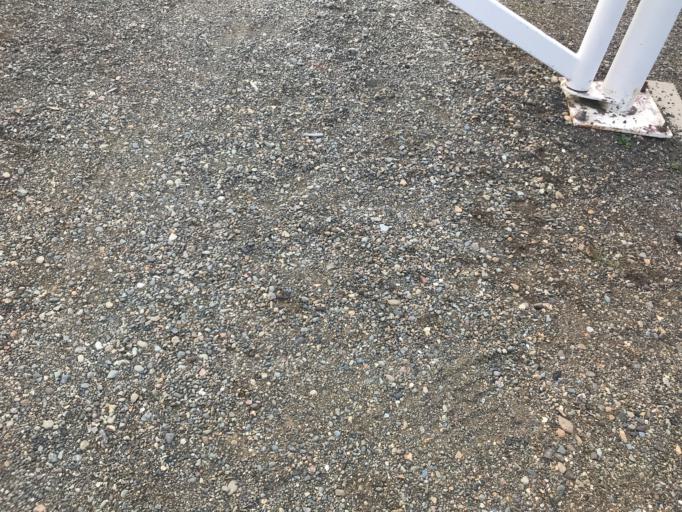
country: US
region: Washington
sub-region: Kittitas County
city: Ellensburg
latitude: 47.0072
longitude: -120.5507
